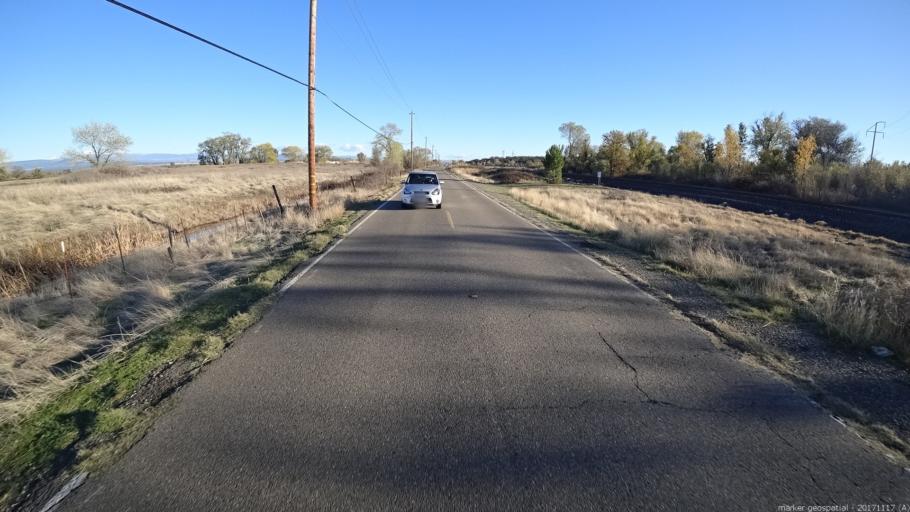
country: US
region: California
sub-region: Shasta County
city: Anderson
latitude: 40.4253
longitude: -122.2636
